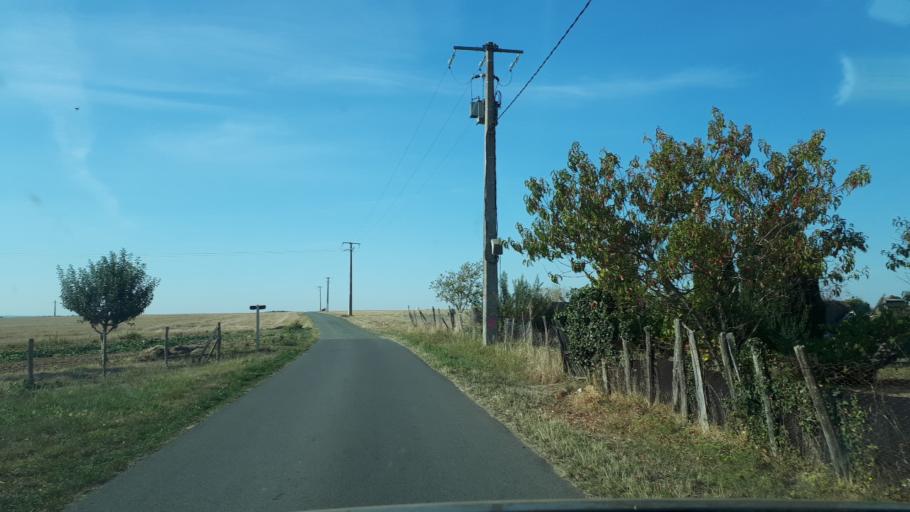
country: FR
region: Centre
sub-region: Departement du Loir-et-Cher
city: Lunay
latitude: 47.8349
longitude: 0.9528
